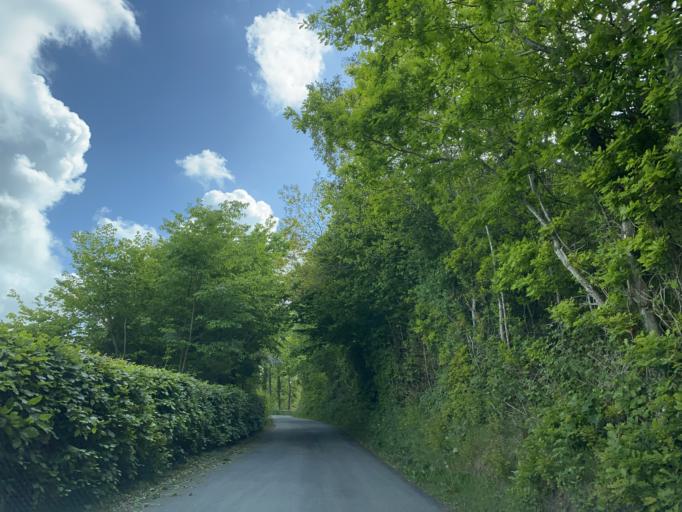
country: DK
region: South Denmark
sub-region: Aabenraa Kommune
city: Lojt Kirkeby
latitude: 55.0101
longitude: 9.4866
